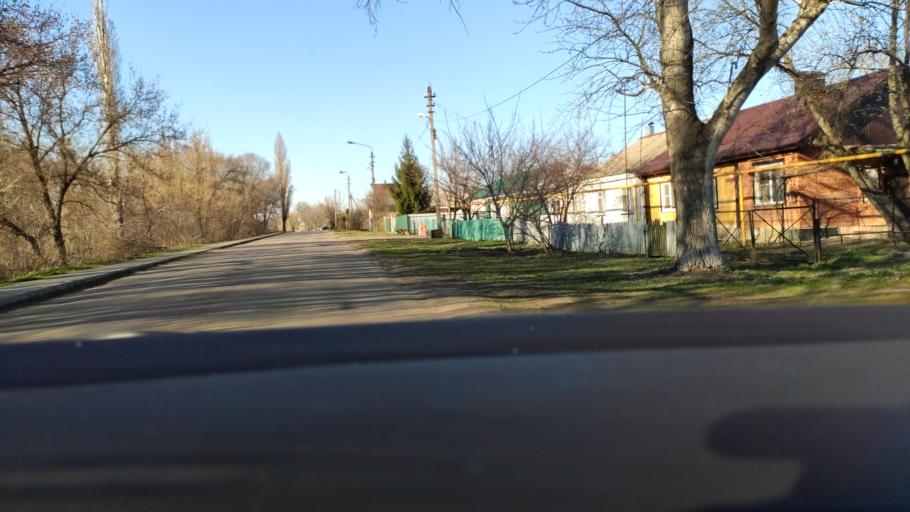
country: RU
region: Voronezj
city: Maslovka
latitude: 51.5039
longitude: 39.2935
